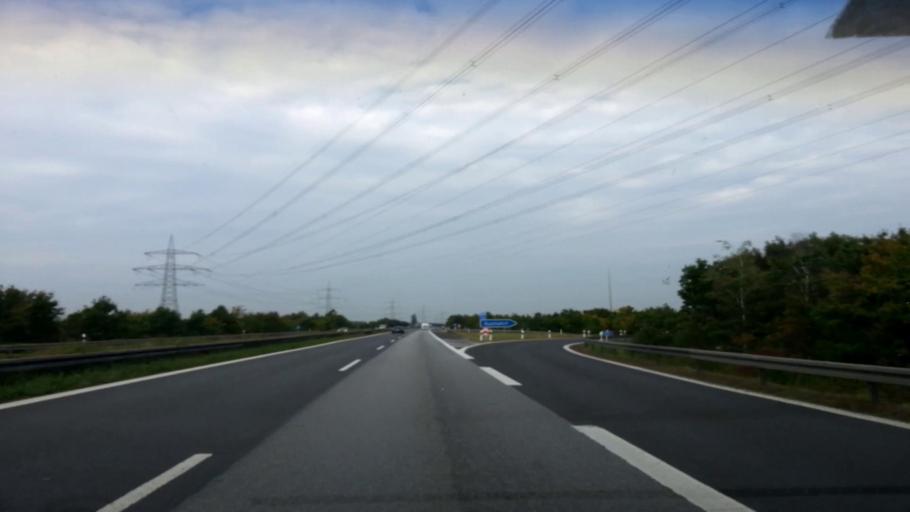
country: DE
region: Bavaria
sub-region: Regierungsbezirk Unterfranken
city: Knetzgau
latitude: 49.9780
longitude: 10.5620
